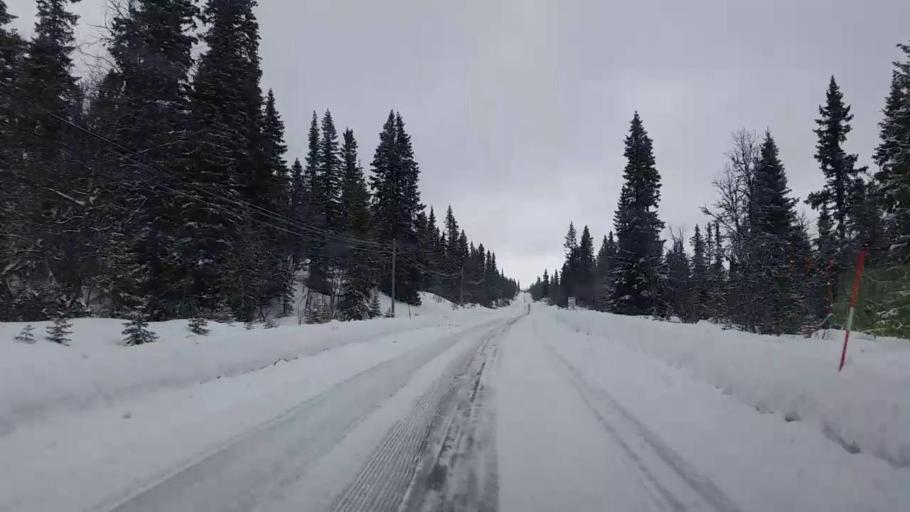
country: SE
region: Jaemtland
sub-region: Bergs Kommun
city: Hoverberg
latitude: 62.4826
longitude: 14.1219
